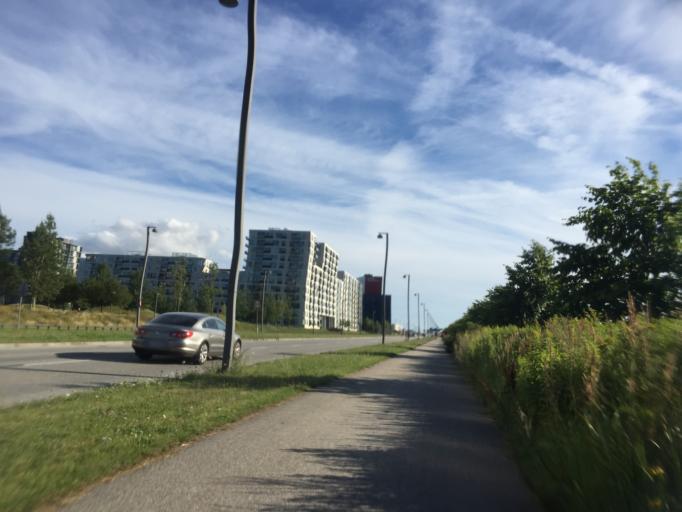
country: DK
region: Capital Region
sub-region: Tarnby Kommune
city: Tarnby
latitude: 55.6353
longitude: 12.5734
